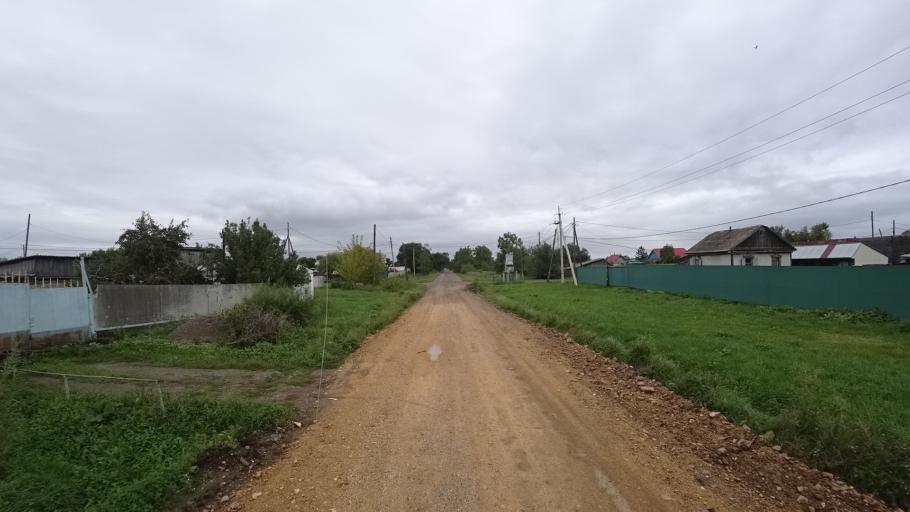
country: RU
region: Primorskiy
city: Chernigovka
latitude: 44.3382
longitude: 132.5608
